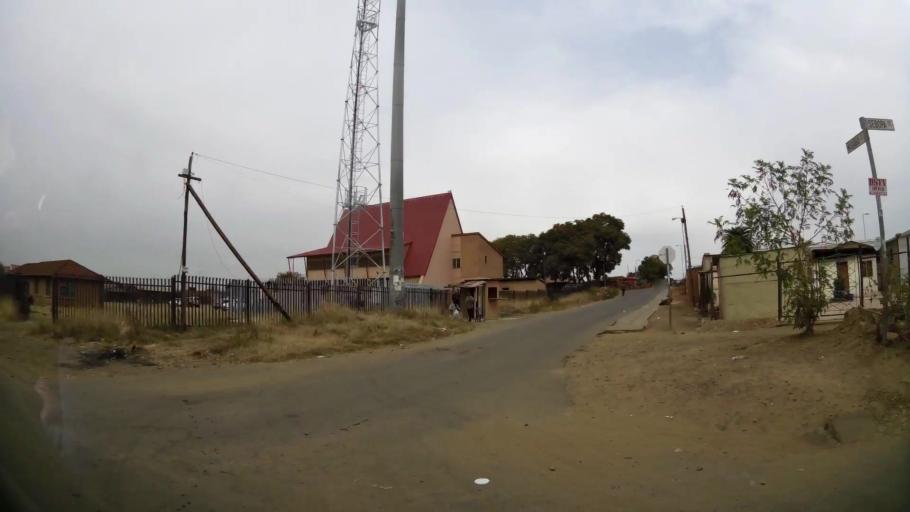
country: ZA
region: Gauteng
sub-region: City of Tshwane Metropolitan Municipality
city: Pretoria
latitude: -25.7086
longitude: 28.3497
